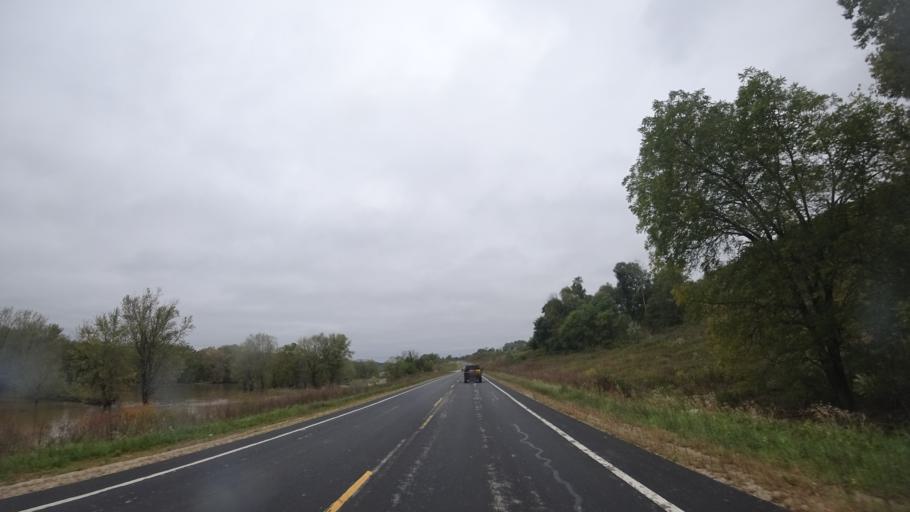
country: US
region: Wisconsin
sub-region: Grant County
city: Boscobel
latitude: 43.1173
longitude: -90.7879
